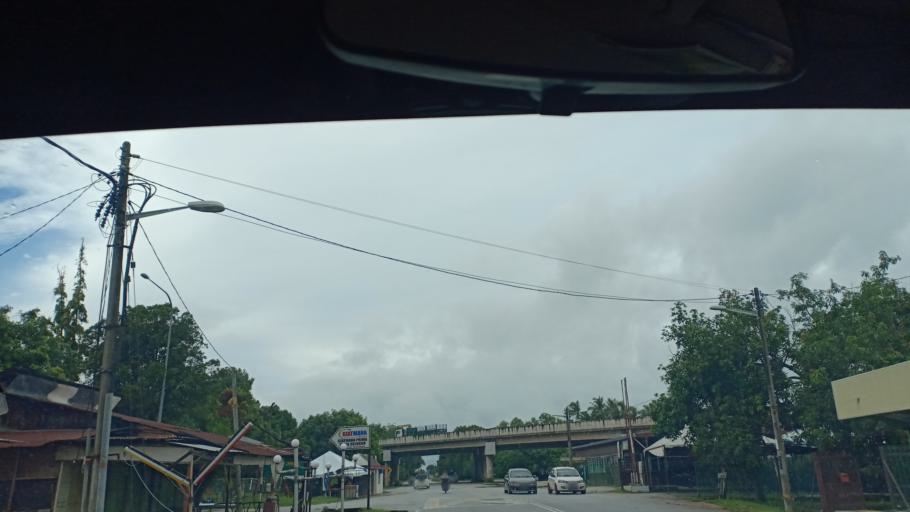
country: MY
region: Penang
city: Kepala Batas
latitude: 5.4971
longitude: 100.4371
